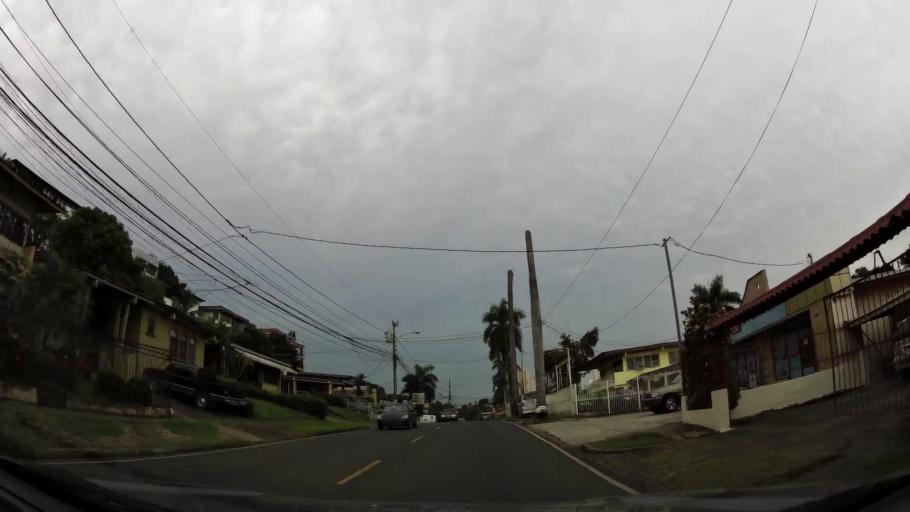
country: PA
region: Panama
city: Panama
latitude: 9.0146
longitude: -79.5245
